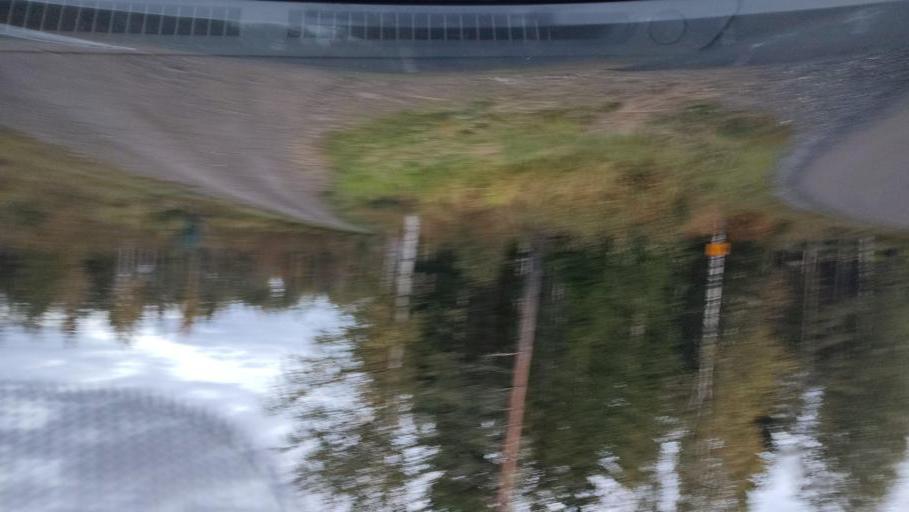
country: FI
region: Ostrobothnia
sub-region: Sydosterbotten
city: Kristinestad
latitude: 62.2802
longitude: 21.5150
